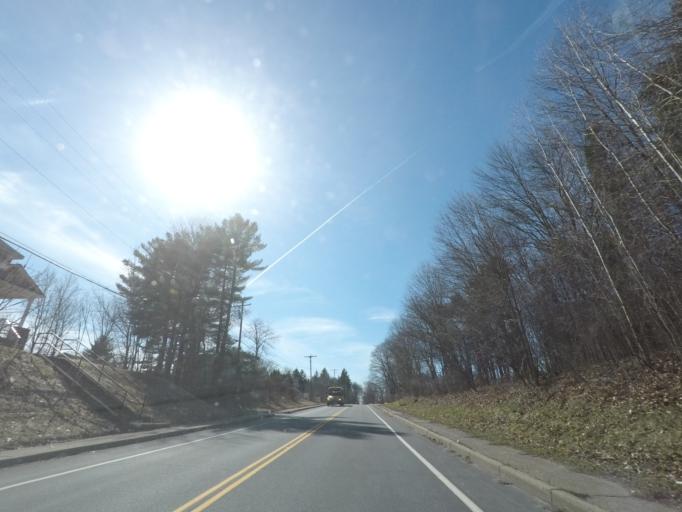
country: US
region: New York
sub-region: Saratoga County
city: Ballston Spa
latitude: 43.0015
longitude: -73.8387
